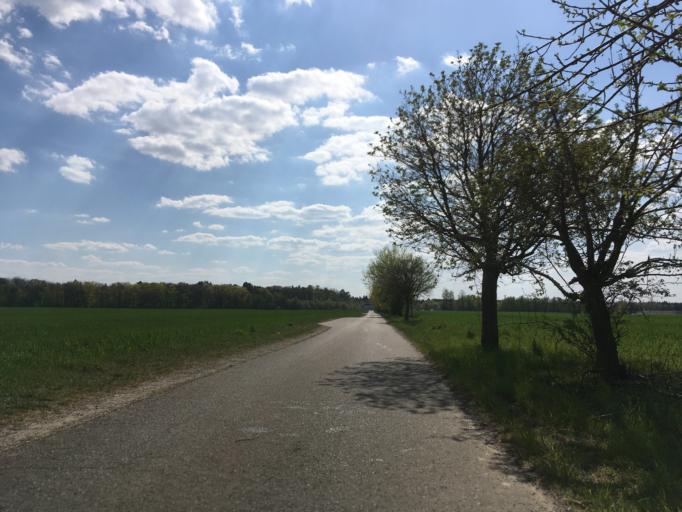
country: DE
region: Brandenburg
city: Ahrensfelde
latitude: 52.6010
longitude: 13.5910
